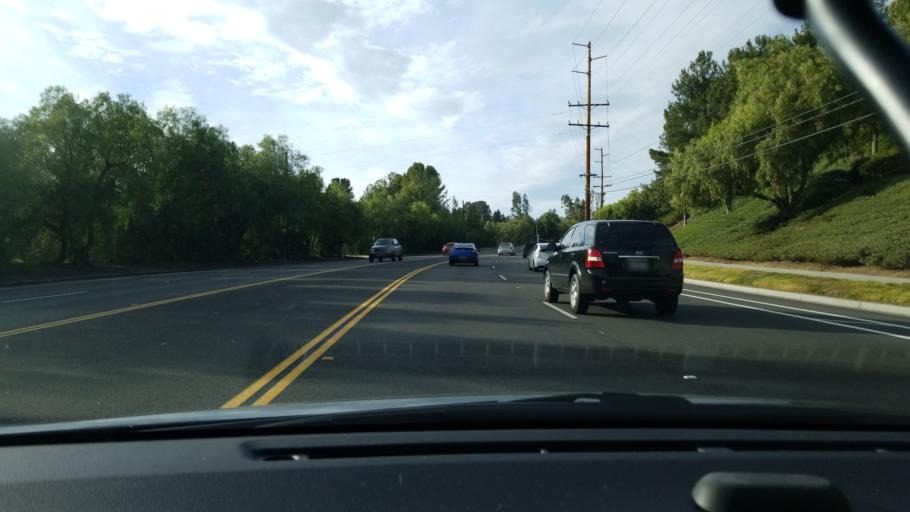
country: US
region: California
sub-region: Riverside County
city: Temecula
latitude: 33.4883
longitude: -117.1080
